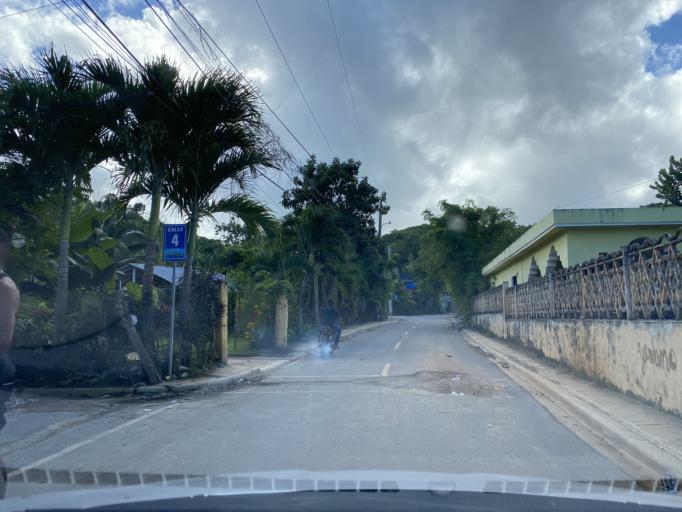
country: DO
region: Samana
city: Las Terrenas
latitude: 19.3042
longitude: -69.5420
